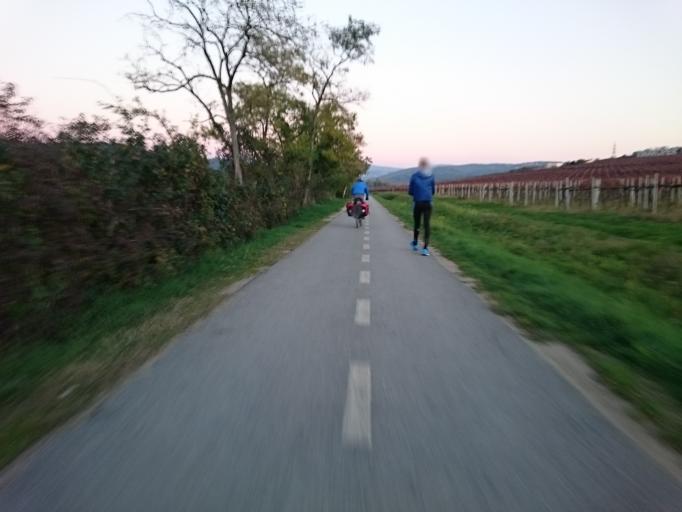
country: SI
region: Koper-Capodistria
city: Prade
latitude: 45.5498
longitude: 13.7759
